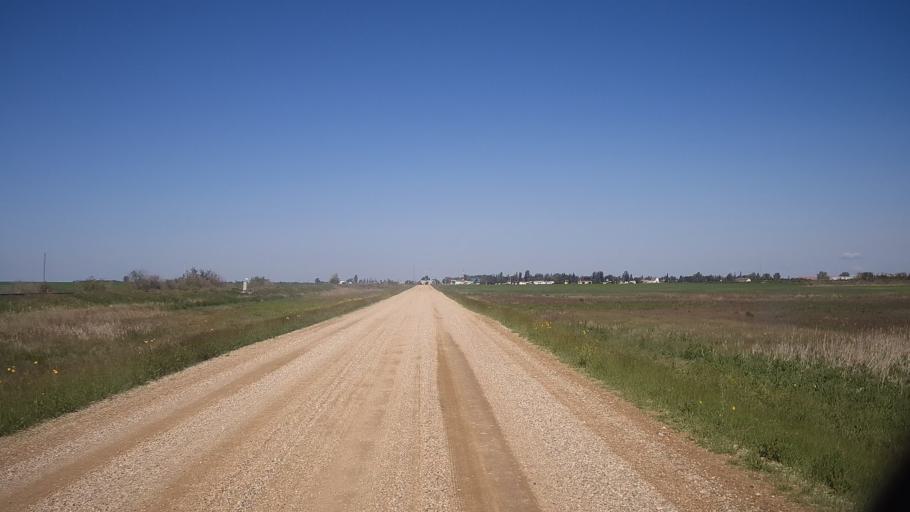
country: CA
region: Saskatchewan
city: Watrous
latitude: 51.8863
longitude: -106.0377
